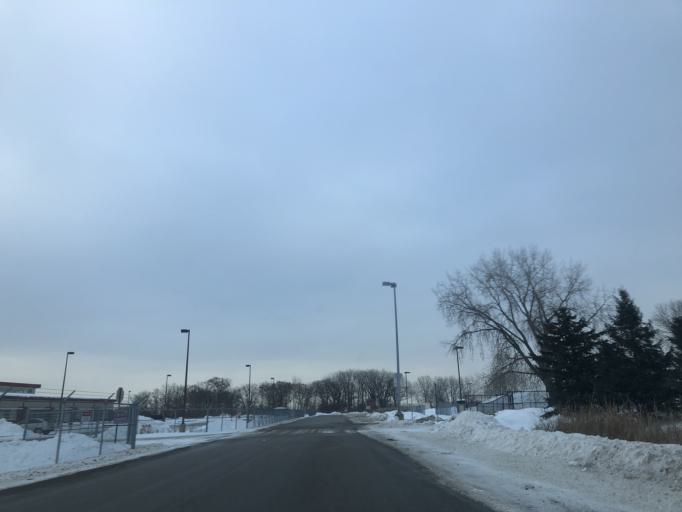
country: US
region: Minnesota
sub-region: Ramsey County
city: Shoreview
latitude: 45.0832
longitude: -93.1609
